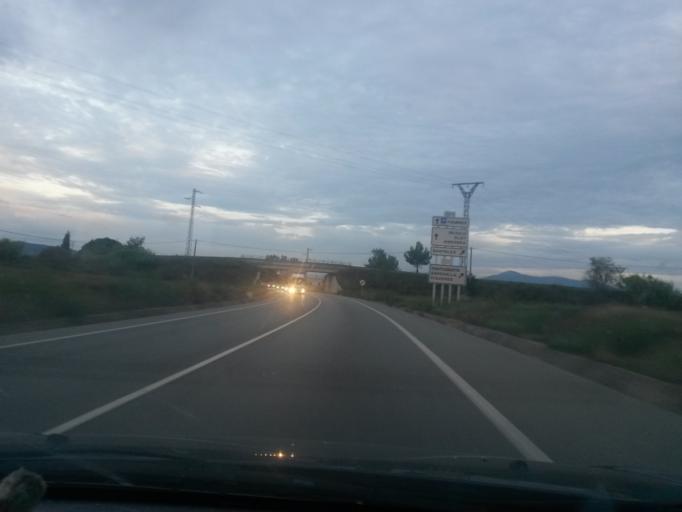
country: ES
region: Catalonia
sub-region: Provincia de Girona
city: Banyoles
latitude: 42.1357
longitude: 2.7725
